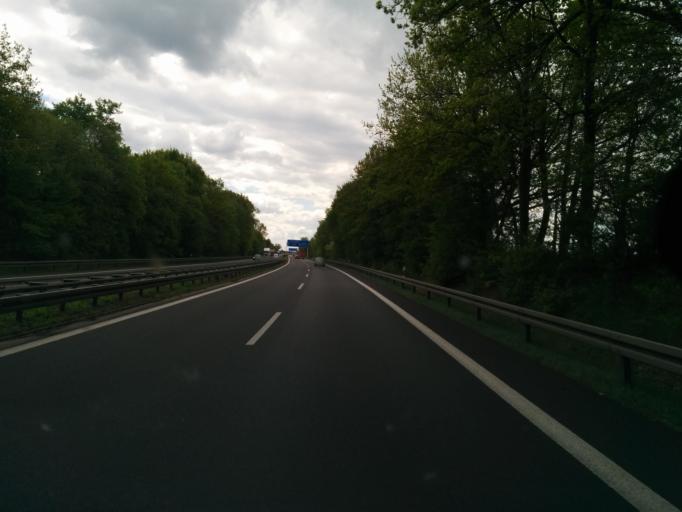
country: DE
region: Brandenburg
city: Gross Kreutz
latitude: 52.3591
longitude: 12.8149
